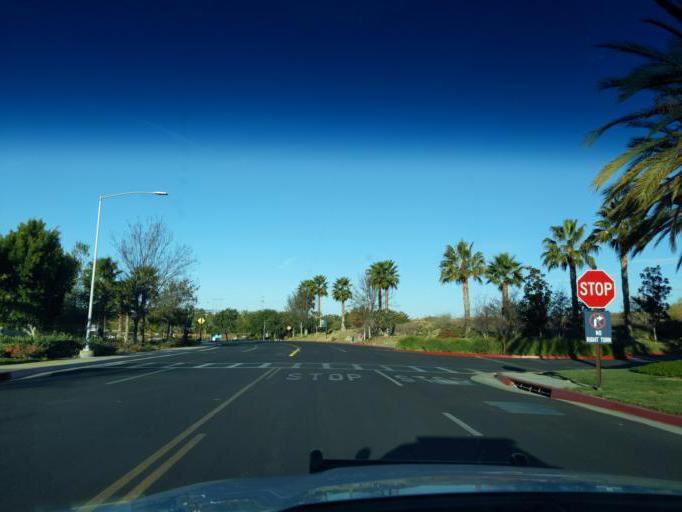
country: US
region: California
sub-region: Orange County
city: Portola Hills
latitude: 33.6638
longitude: -117.6502
